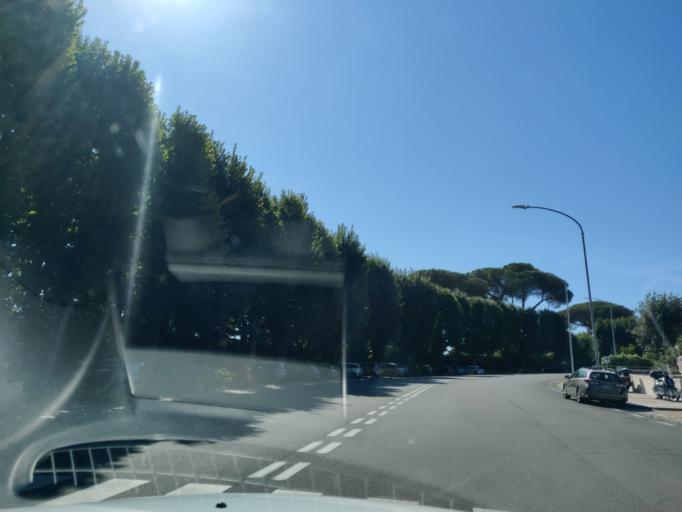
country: IT
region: Latium
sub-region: Citta metropolitana di Roma Capitale
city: Rome
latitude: 41.8370
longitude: 12.4749
